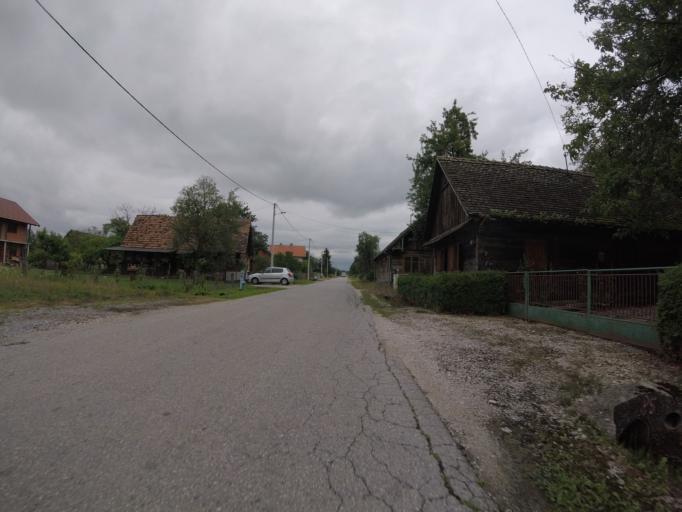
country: HR
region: Zagrebacka
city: Turopolje
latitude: 45.6366
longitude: 16.1217
